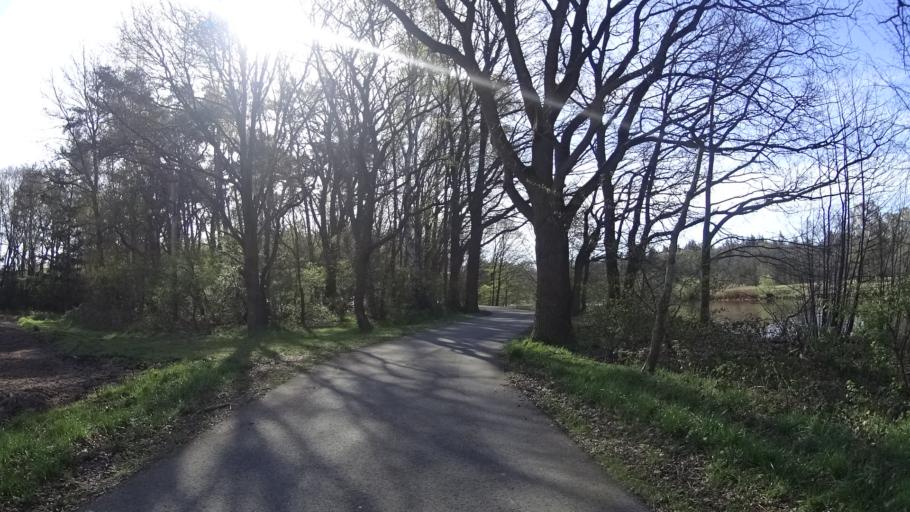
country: DE
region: Lower Saxony
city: Meppen
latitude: 52.7164
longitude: 7.2712
